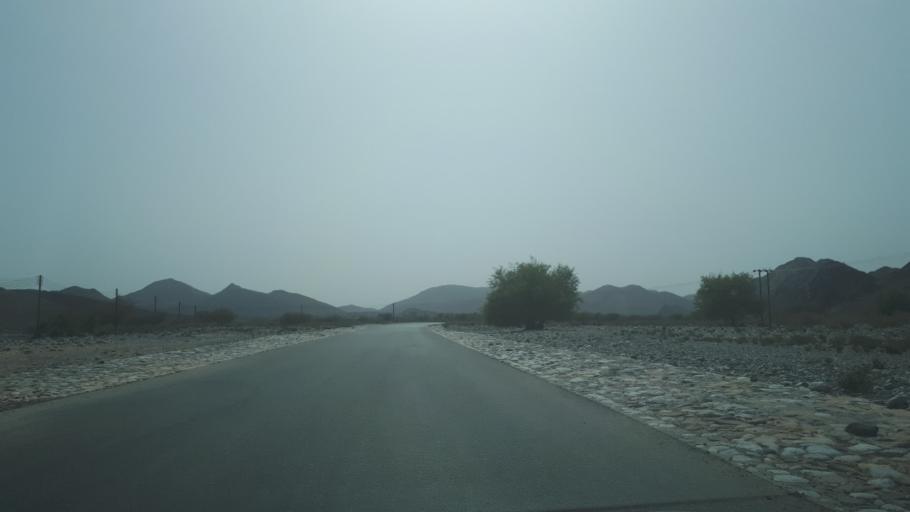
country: OM
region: Muhafazat ad Dakhiliyah
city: Bahla'
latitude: 23.2184
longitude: 57.0084
